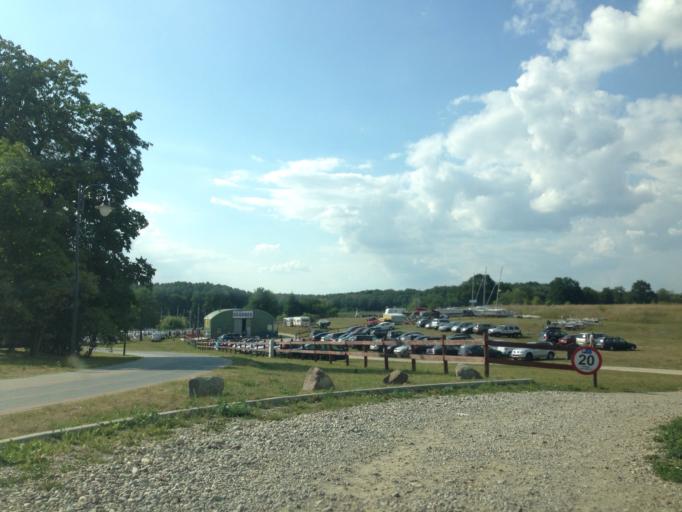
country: PL
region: Warmian-Masurian Voivodeship
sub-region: Powiat ilawski
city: Ilawa
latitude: 53.6168
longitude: 19.5658
